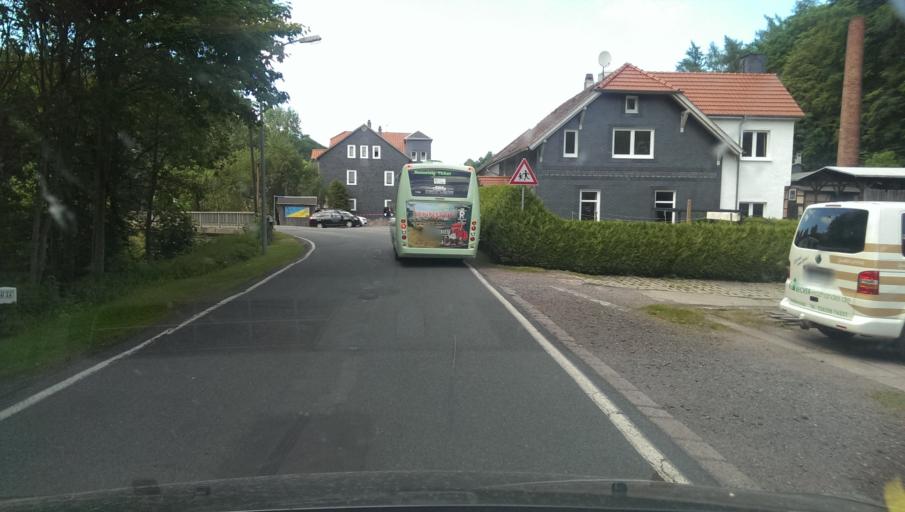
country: DE
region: Thuringia
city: Grafenroda
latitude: 50.7297
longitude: 10.7925
